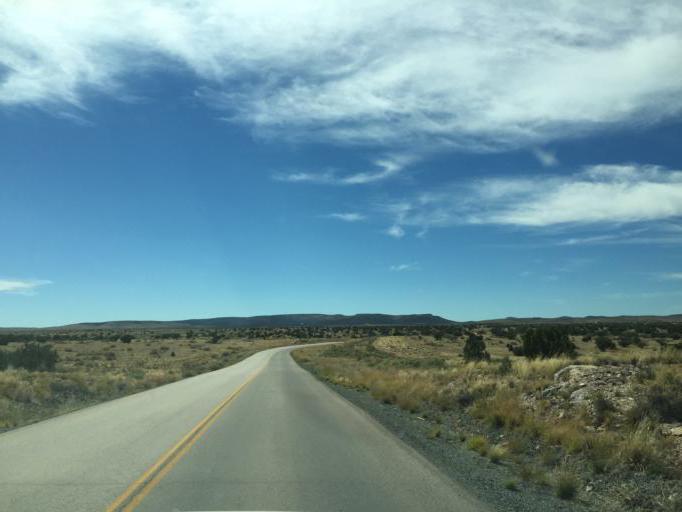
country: US
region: Arizona
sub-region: Mohave County
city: Meadview
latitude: 35.9633
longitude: -113.8254
